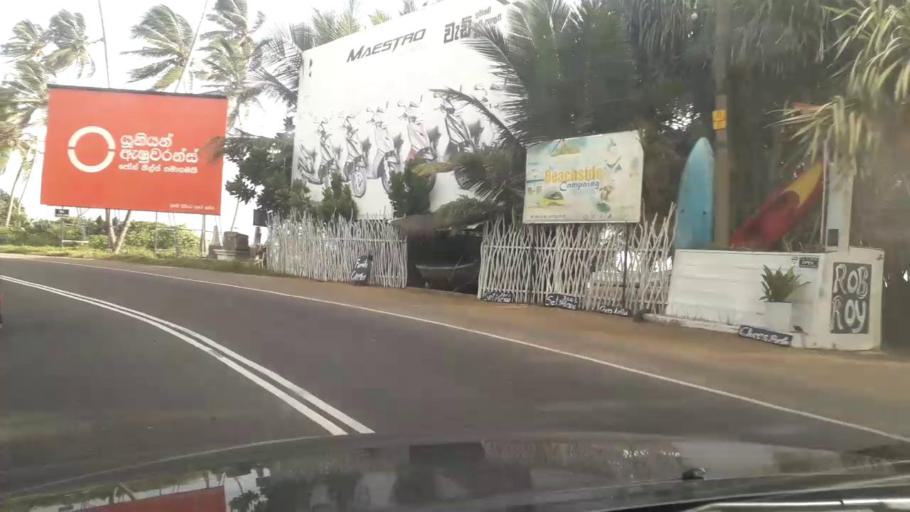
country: LK
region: Western
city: Beruwala
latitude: 6.5205
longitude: 79.9790
